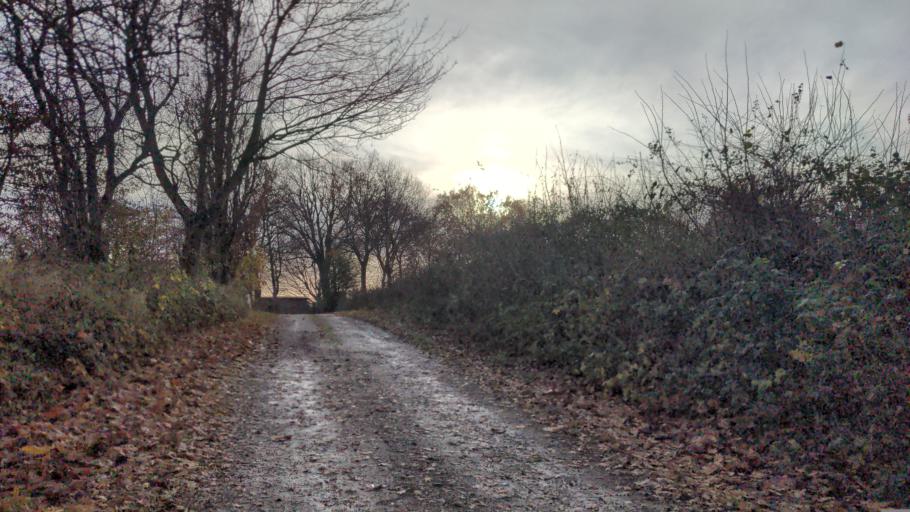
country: DE
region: Schleswig-Holstein
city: Neustadt in Holstein
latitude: 54.0889
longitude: 10.7936
